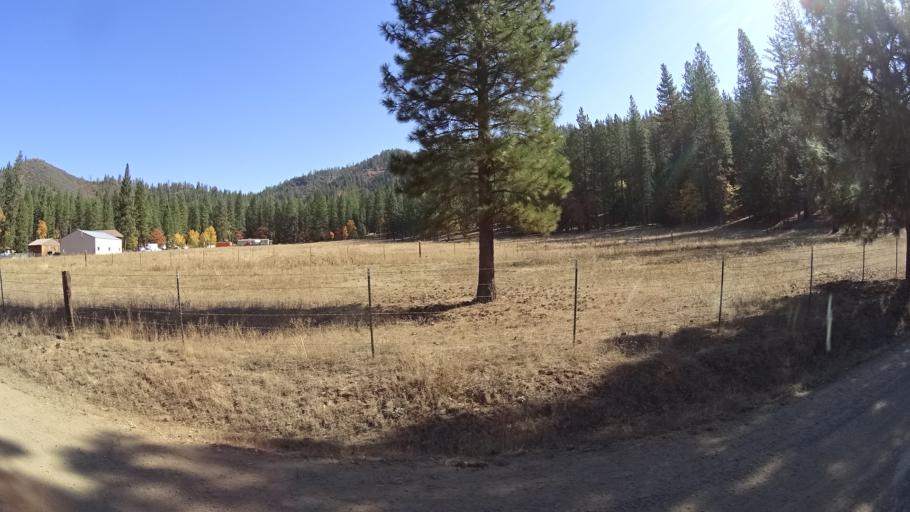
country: US
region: California
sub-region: Siskiyou County
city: Yreka
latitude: 41.6006
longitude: -122.9574
